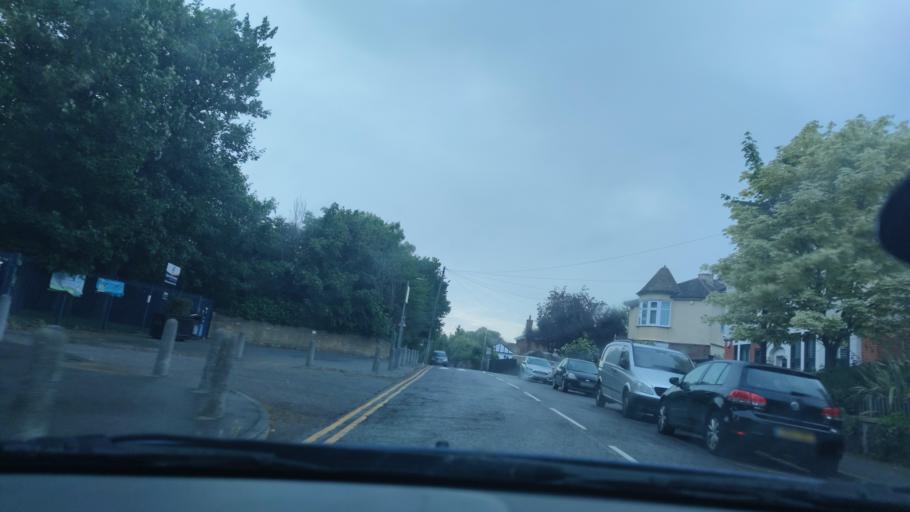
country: GB
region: England
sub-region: Borough of Thurrock
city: Grays
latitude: 51.4818
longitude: 0.3317
